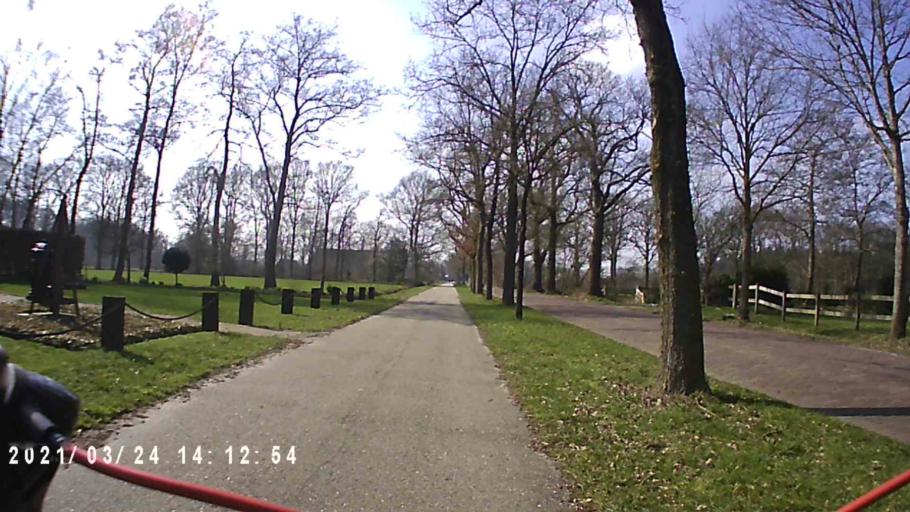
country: NL
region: Friesland
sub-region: Gemeente Smallingerland
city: Drachtstercompagnie
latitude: 53.0651
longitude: 6.2203
